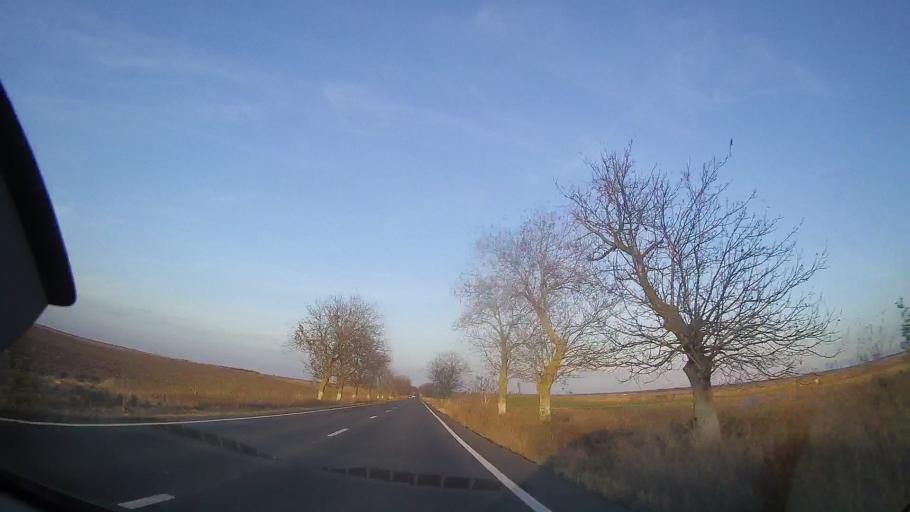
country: RO
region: Constanta
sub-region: Comuna Amzacea
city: Amzacea
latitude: 43.9431
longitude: 28.3736
